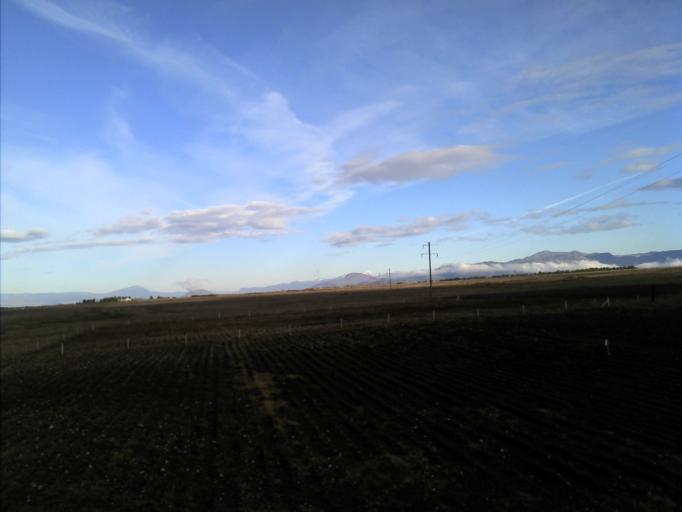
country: AL
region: Shkoder
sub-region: Rrethi i Malesia e Madhe
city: Koplik
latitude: 42.2221
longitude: 19.4393
